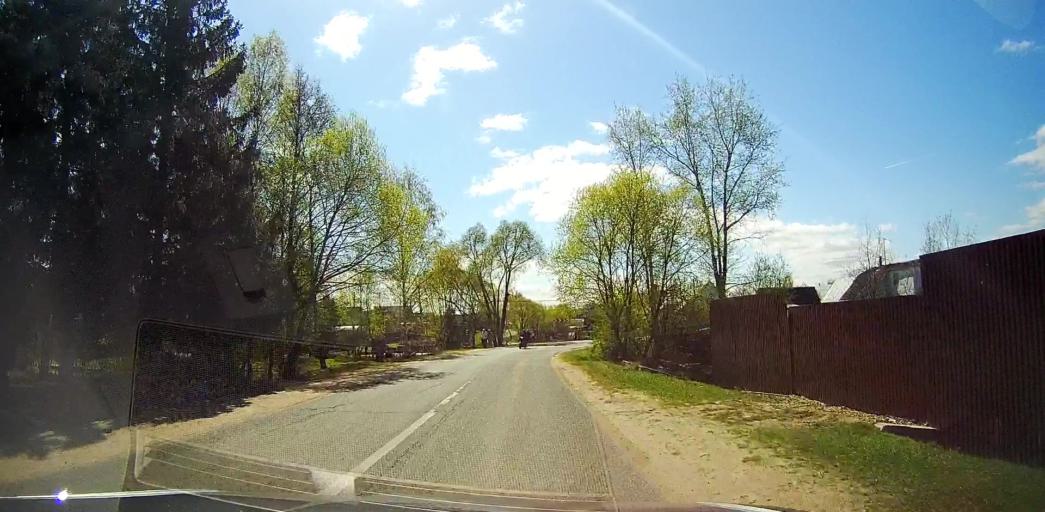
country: RU
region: Moskovskaya
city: Ramenskoye
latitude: 55.6143
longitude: 38.3043
